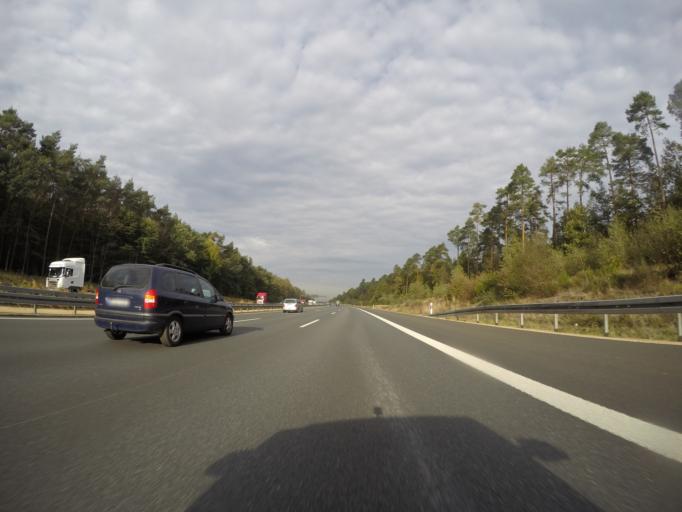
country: DE
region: Bavaria
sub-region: Regierungsbezirk Mittelfranken
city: Heroldsberg
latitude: 49.5073
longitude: 11.1153
